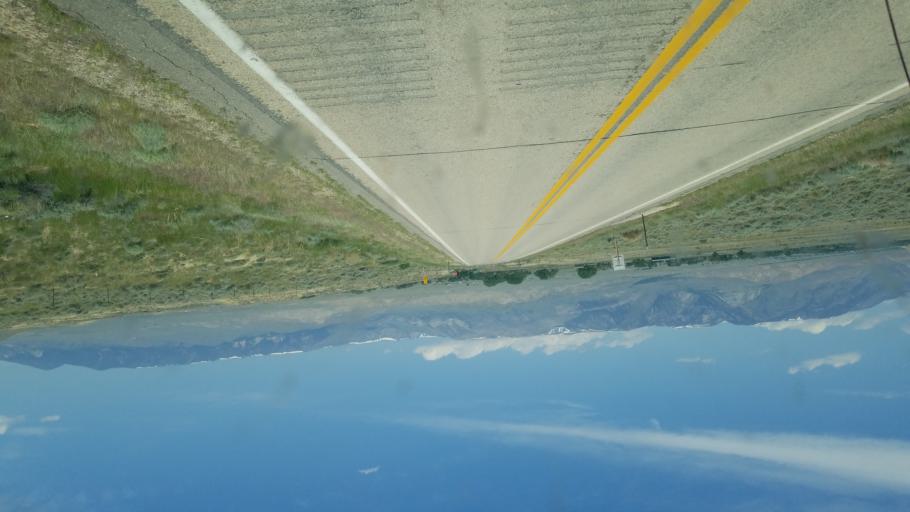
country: US
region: Montana
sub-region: Carbon County
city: Red Lodge
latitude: 44.9010
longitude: -109.1013
